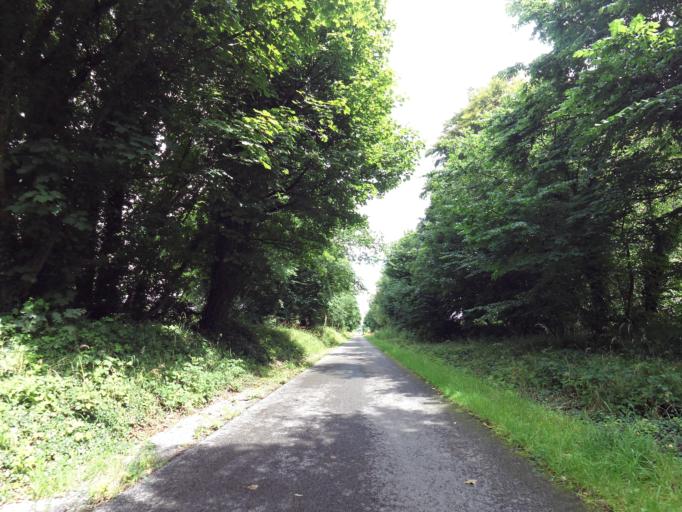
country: IE
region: Leinster
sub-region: An Iarmhi
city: Kilbeggan
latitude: 53.4643
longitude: -7.5043
